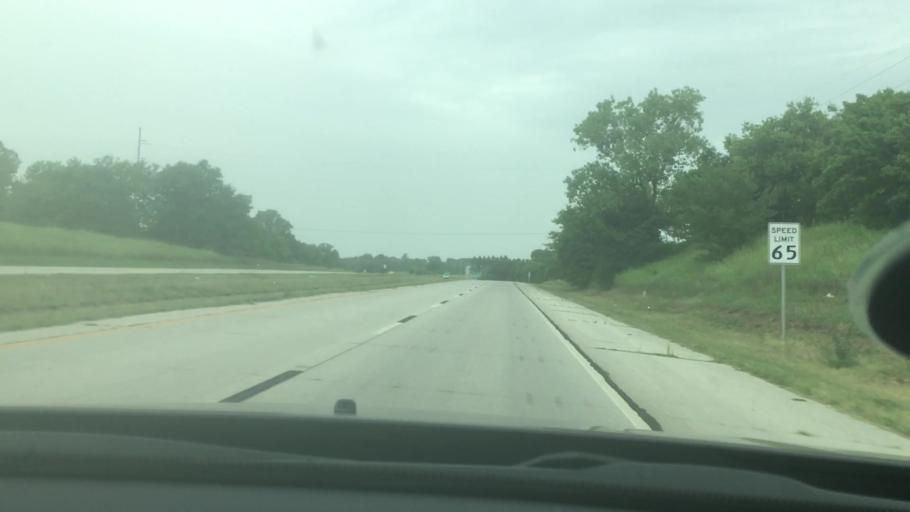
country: US
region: Oklahoma
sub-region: Pontotoc County
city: Ada
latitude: 34.7506
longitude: -96.6589
